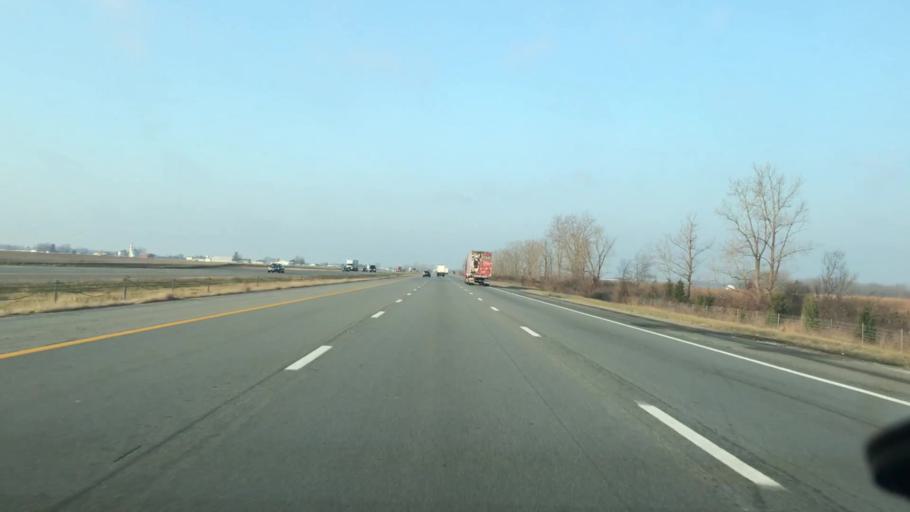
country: US
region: Ohio
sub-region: Madison County
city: Choctaw Lake
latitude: 39.9456
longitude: -83.4254
